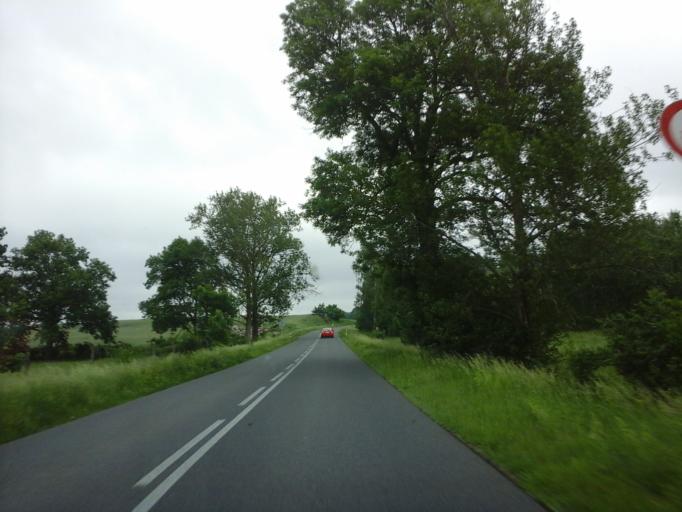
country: PL
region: West Pomeranian Voivodeship
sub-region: Powiat walecki
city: Miroslawiec
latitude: 53.3512
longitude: 16.1049
